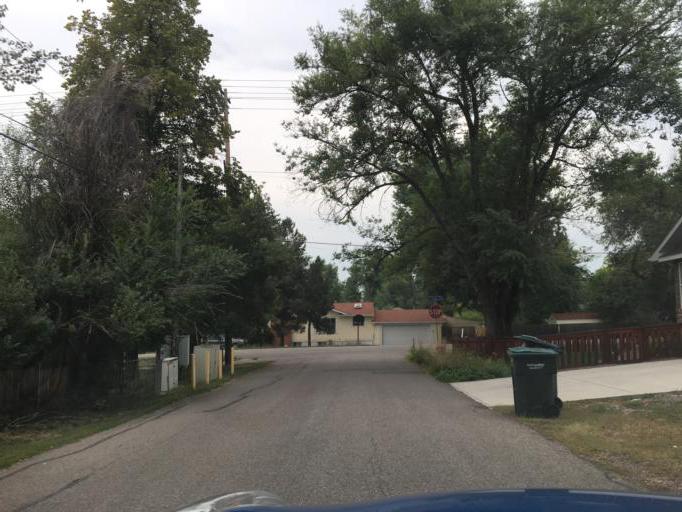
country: US
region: Colorado
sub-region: Jefferson County
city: Wheat Ridge
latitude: 39.7480
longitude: -105.0964
